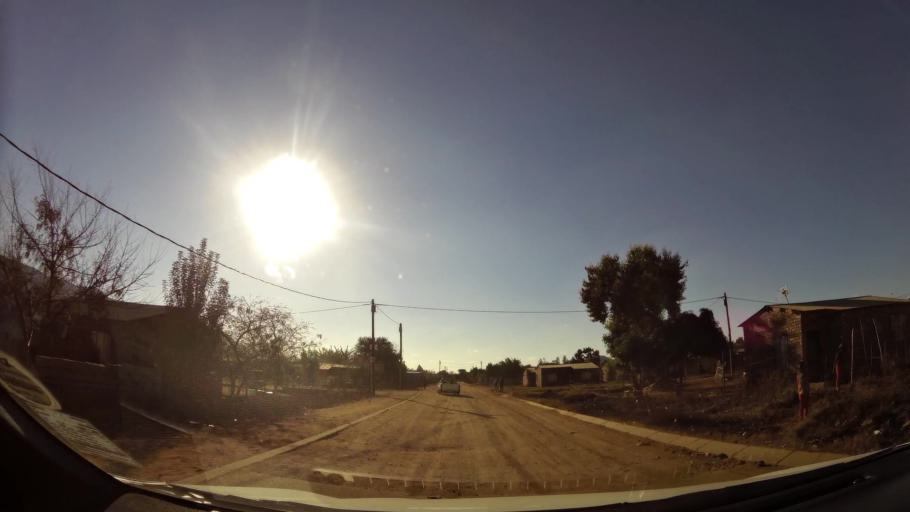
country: ZA
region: Limpopo
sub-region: Waterberg District Municipality
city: Mokopane
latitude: -24.1886
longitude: 28.9782
